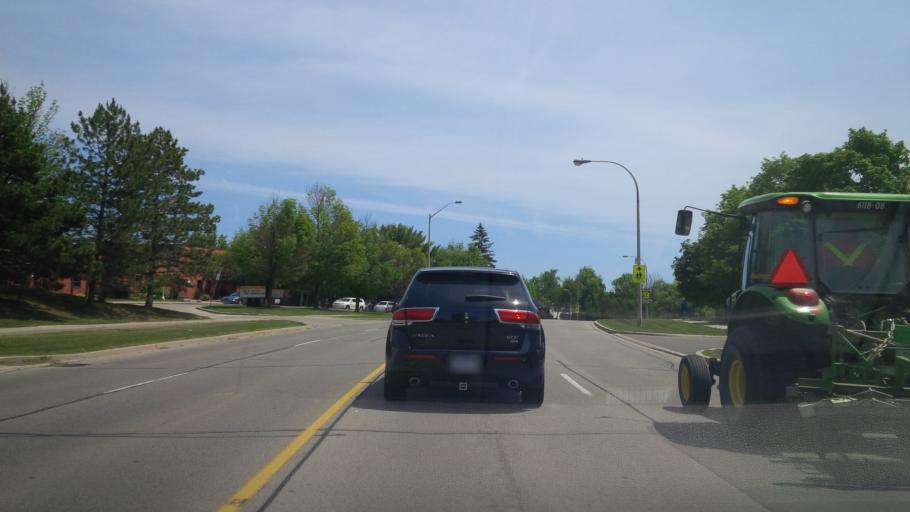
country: CA
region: Ontario
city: Burlington
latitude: 43.3597
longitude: -79.8406
